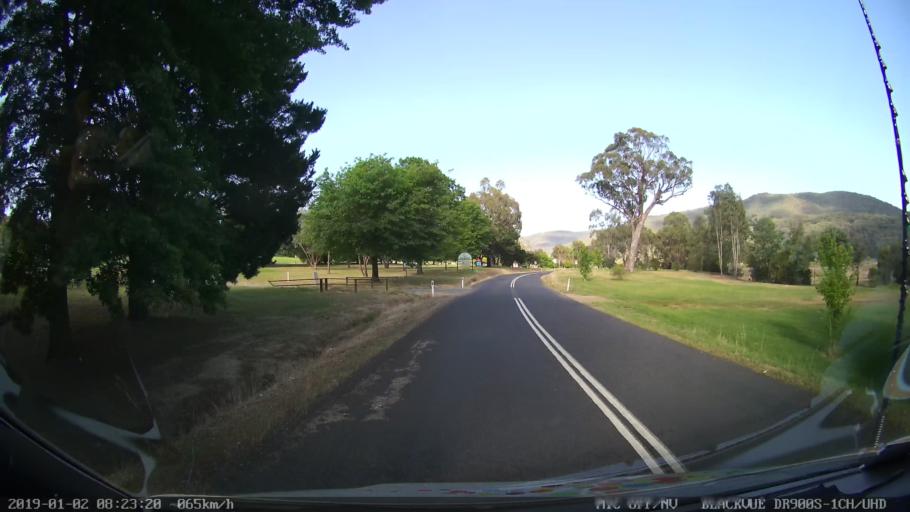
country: AU
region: New South Wales
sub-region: Tumut Shire
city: Tumut
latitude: -35.5781
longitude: 148.3080
